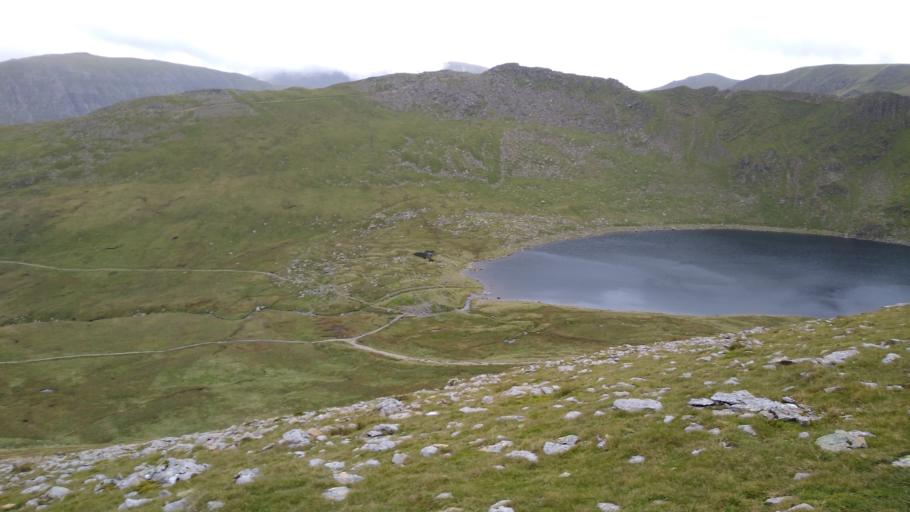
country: GB
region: England
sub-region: Cumbria
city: Ambleside
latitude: 54.5334
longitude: -3.0070
